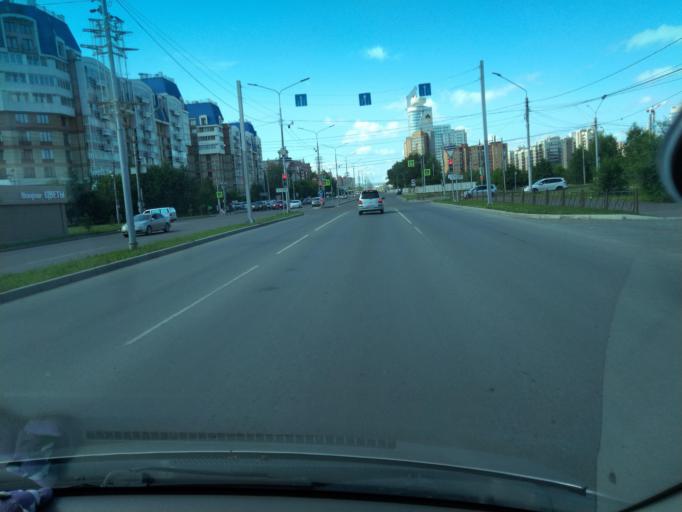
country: RU
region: Krasnoyarskiy
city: Krasnoyarsk
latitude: 56.0472
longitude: 92.9163
